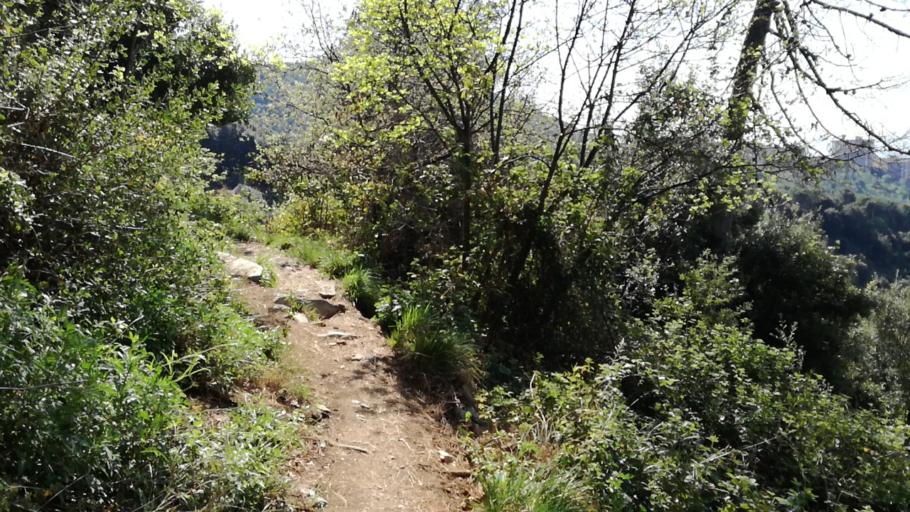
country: IT
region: Liguria
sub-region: Provincia di Genova
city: Genoa
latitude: 44.4352
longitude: 8.9234
